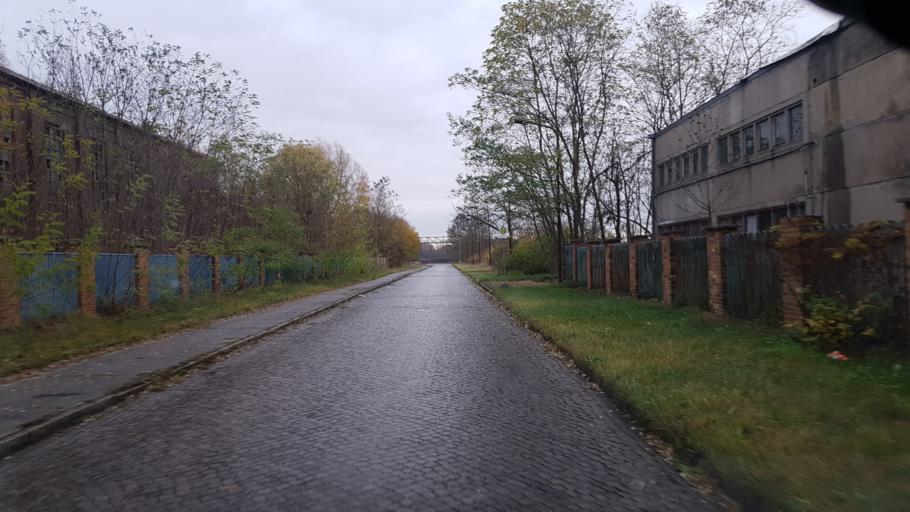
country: DE
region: Brandenburg
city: Lauchhammer
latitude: 51.4920
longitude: 13.7313
